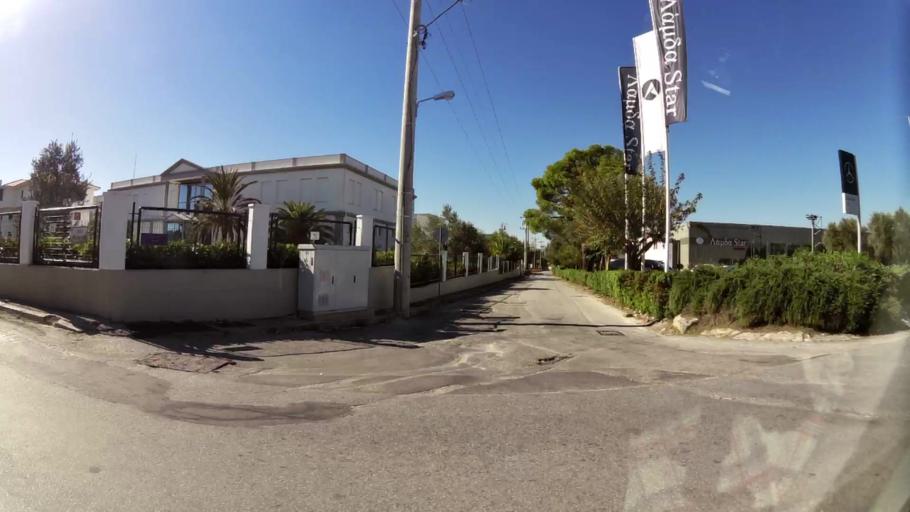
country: GR
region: Attica
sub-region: Nomarchia Athinas
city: Lykovrysi
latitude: 38.0841
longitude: 23.7909
